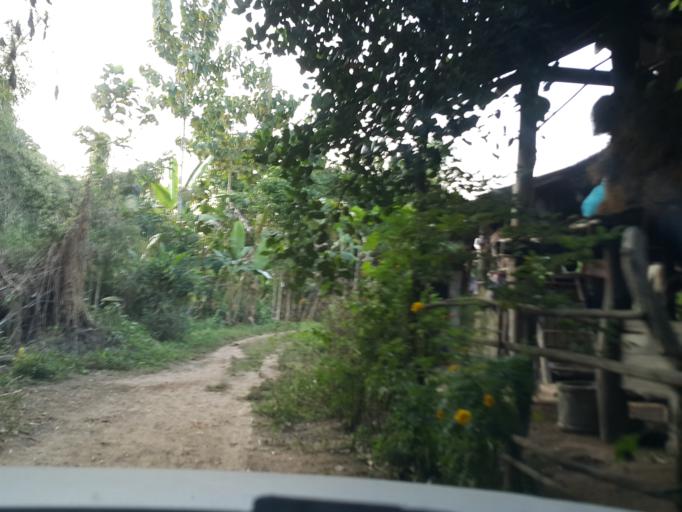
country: TH
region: Lamphun
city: Ban Thi
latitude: 18.5869
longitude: 99.2835
